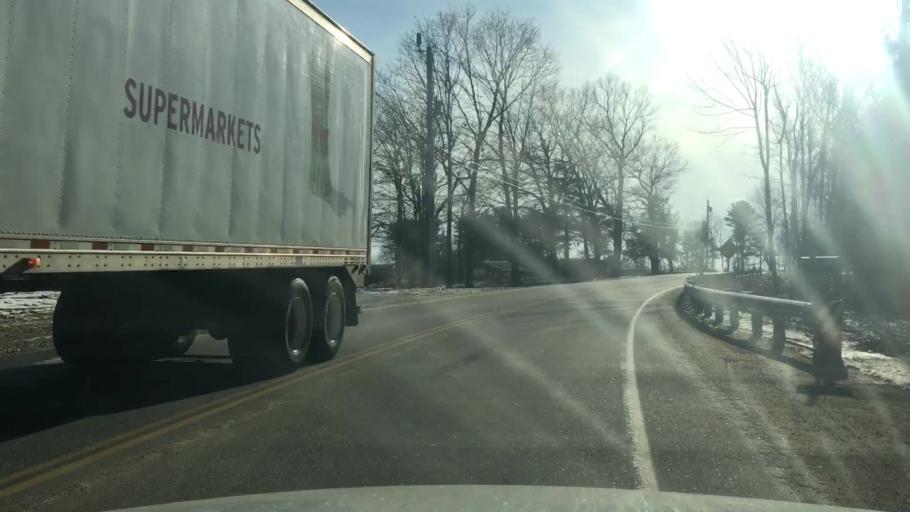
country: US
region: Maine
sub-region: Androscoggin County
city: Sabattus
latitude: 44.1152
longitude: -70.0868
